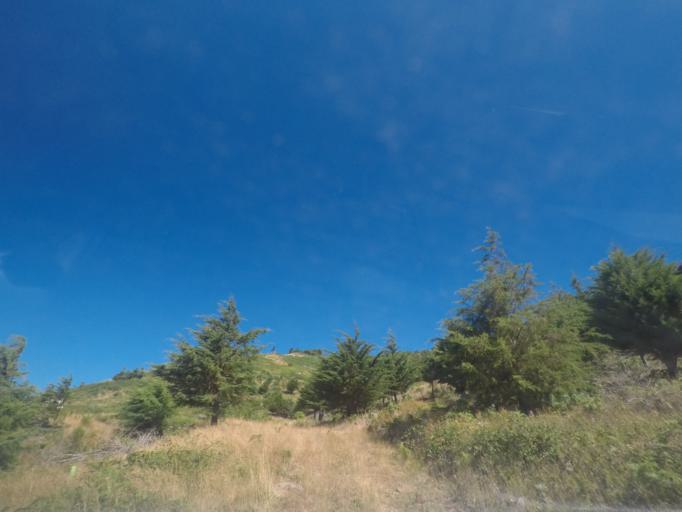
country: PT
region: Madeira
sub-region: Funchal
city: Nossa Senhora do Monte
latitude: 32.7028
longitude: -16.9111
